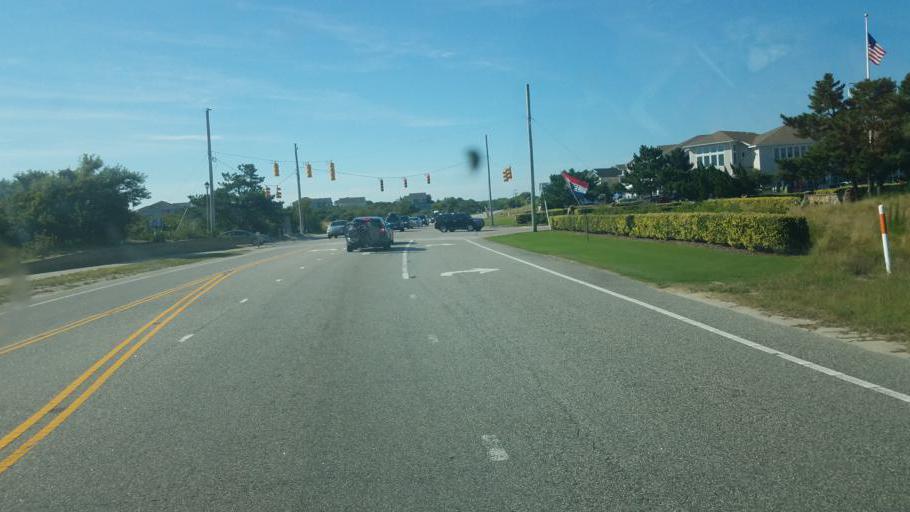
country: US
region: North Carolina
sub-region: Dare County
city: Southern Shores
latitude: 36.3025
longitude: -75.8047
